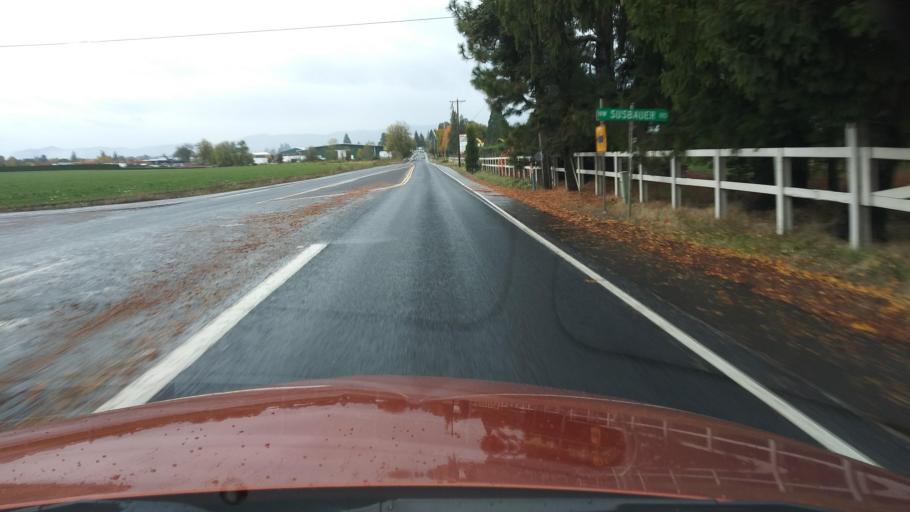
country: US
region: Oregon
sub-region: Washington County
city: North Plains
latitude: 45.5731
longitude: -123.0355
